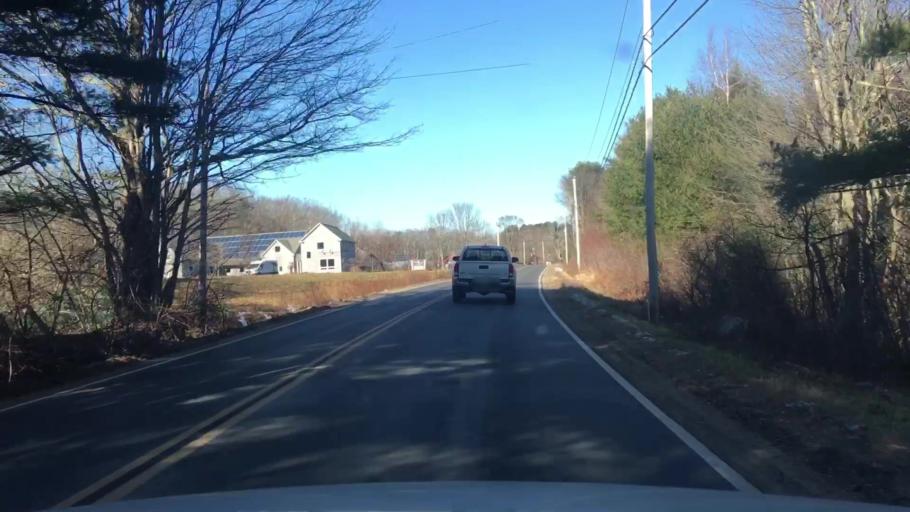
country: US
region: Maine
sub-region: York County
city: Arundel
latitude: 43.4087
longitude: -70.4932
